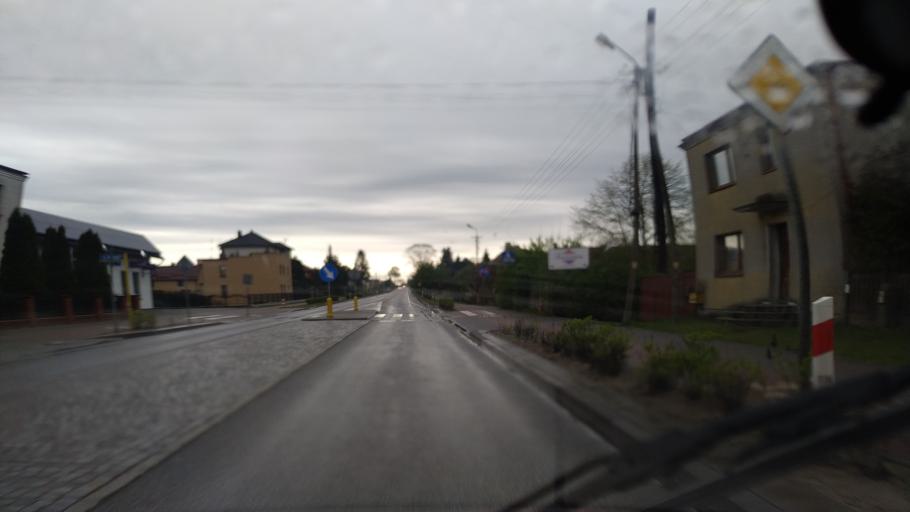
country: PL
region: Pomeranian Voivodeship
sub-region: Powiat chojnicki
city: Czersk
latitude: 53.7971
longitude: 17.9845
